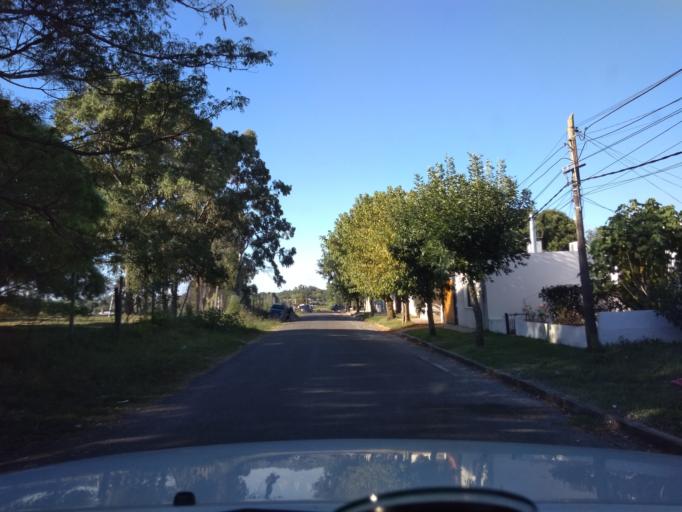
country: UY
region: Florida
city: Florida
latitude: -34.0984
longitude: -56.2273
